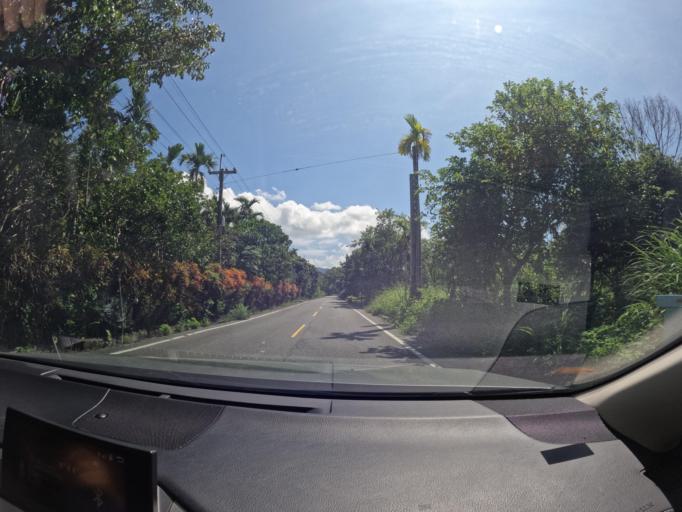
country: TW
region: Taiwan
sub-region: Hualien
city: Hualian
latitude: 23.5869
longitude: 121.3583
